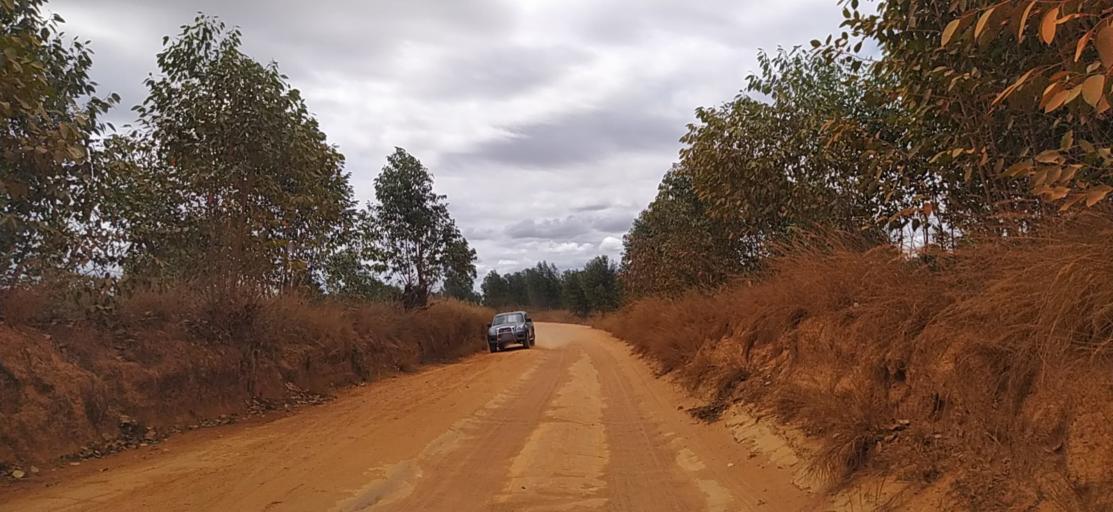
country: MG
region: Alaotra Mangoro
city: Ambatondrazaka
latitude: -18.0441
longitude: 48.2496
